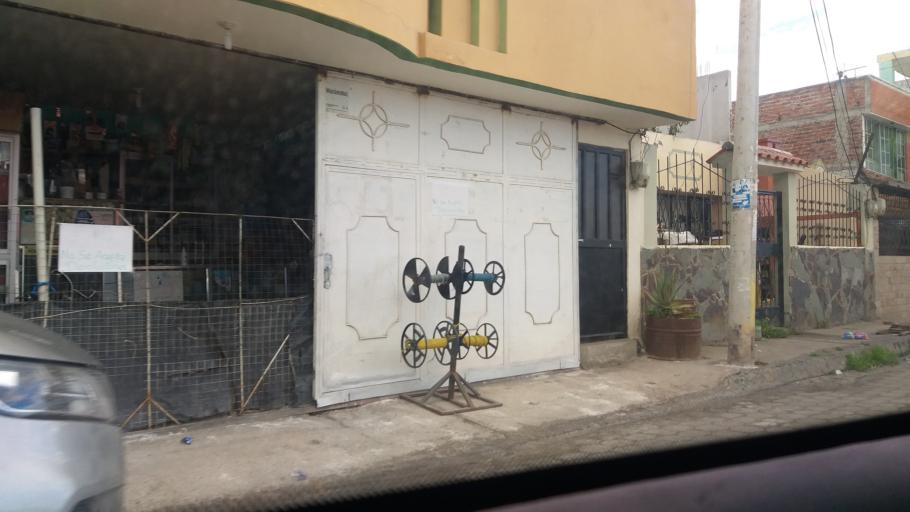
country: EC
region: Chimborazo
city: Riobamba
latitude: -1.6918
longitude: -78.6328
